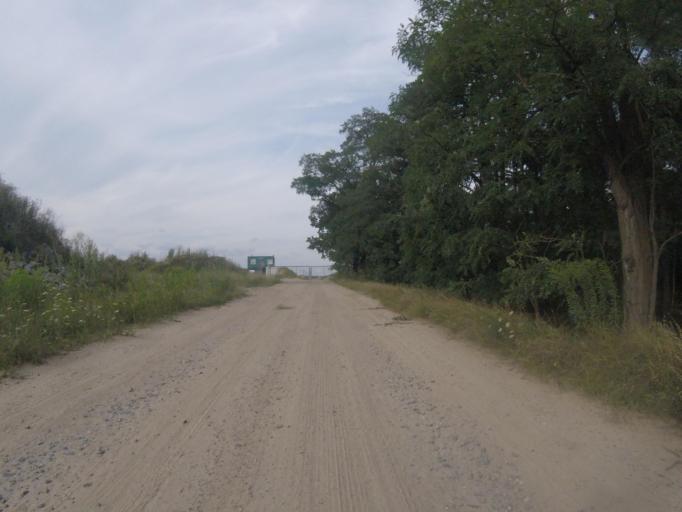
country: DE
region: Brandenburg
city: Rangsdorf
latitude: 52.2784
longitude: 13.4751
